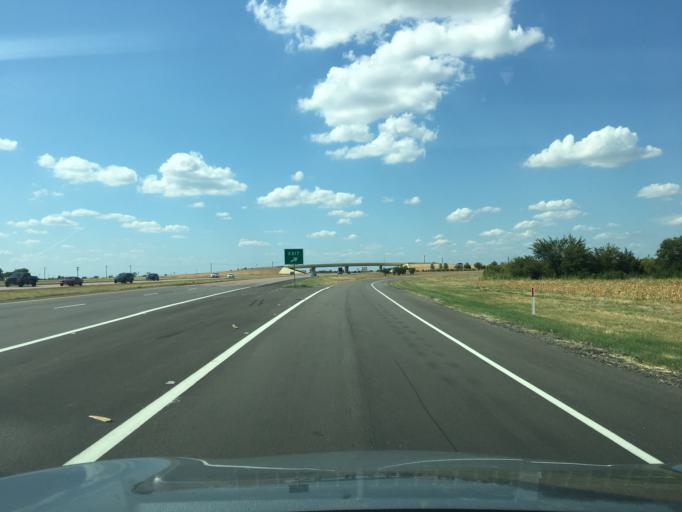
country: US
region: Texas
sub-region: Tarrant County
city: Mansfield
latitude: 32.5336
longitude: -97.1005
